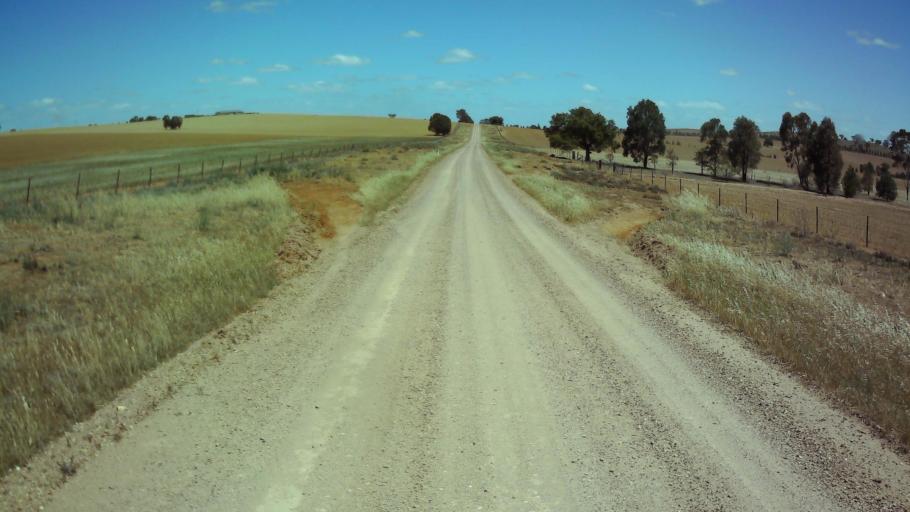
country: AU
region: New South Wales
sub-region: Weddin
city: Grenfell
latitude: -33.9433
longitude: 148.3298
